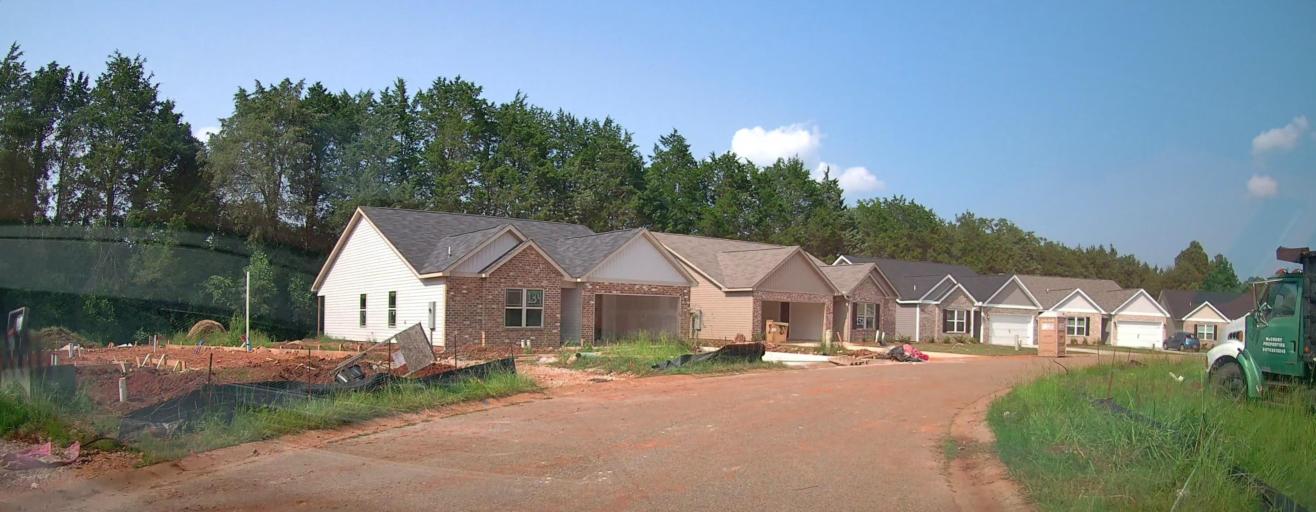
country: US
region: Georgia
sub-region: Houston County
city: Centerville
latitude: 32.6524
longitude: -83.7043
